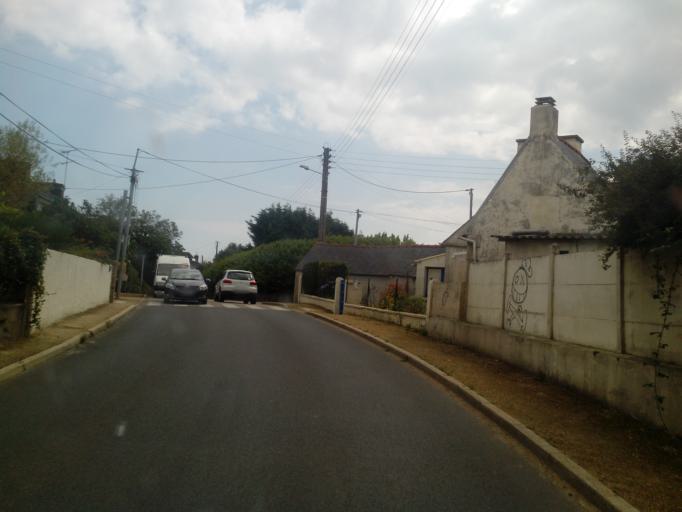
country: FR
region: Brittany
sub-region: Departement des Cotes-d'Armor
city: Plouezec
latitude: 48.7103
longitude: -2.9651
